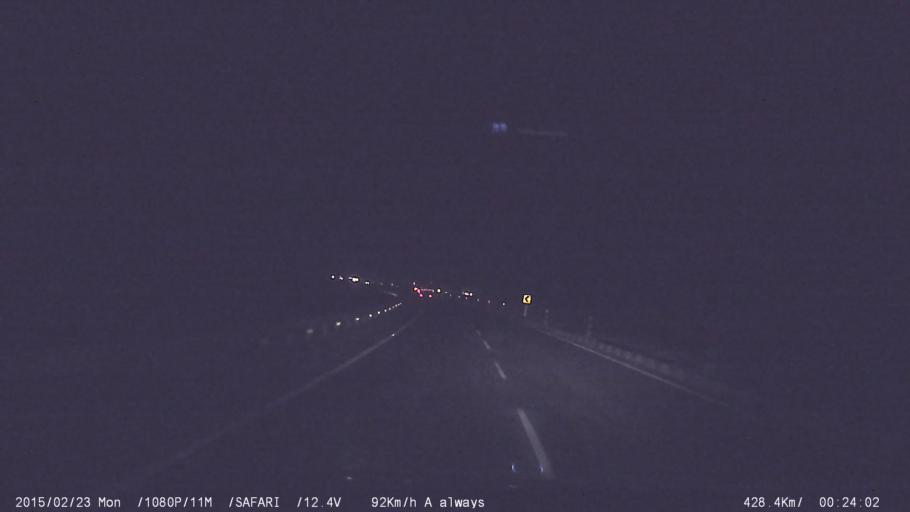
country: IN
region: Tamil Nadu
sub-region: Dharmapuri
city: Mallapuram
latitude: 11.9314
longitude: 78.0648
